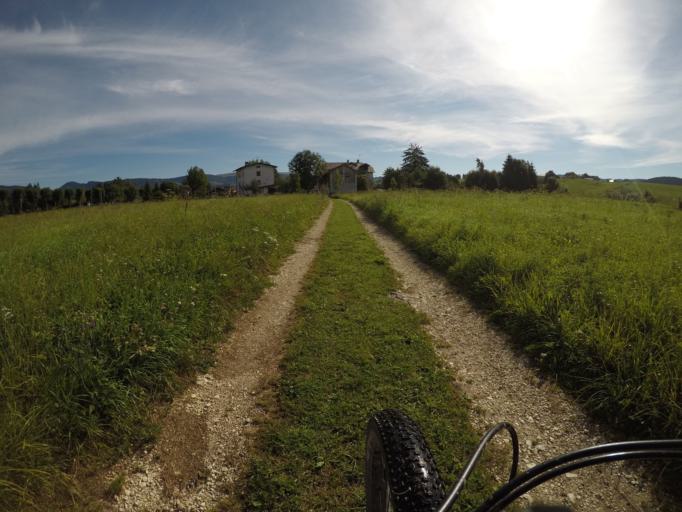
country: IT
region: Veneto
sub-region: Provincia di Vicenza
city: Asiago
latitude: 45.8660
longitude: 11.5045
